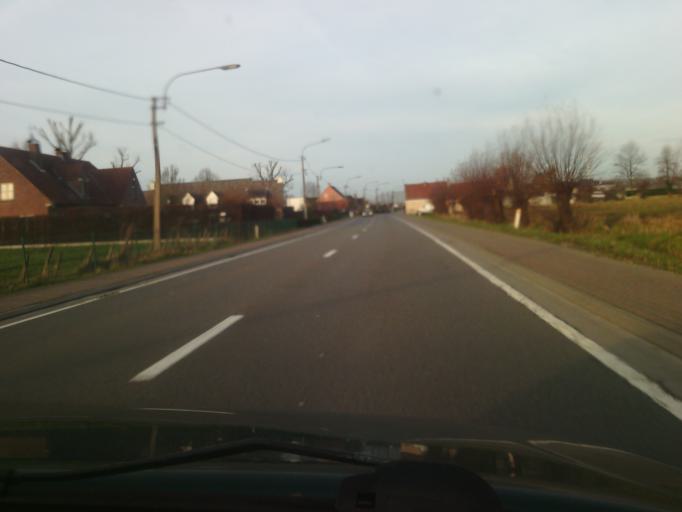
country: BE
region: Flanders
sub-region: Provincie Oost-Vlaanderen
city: Laarne
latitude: 51.0503
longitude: 3.8810
